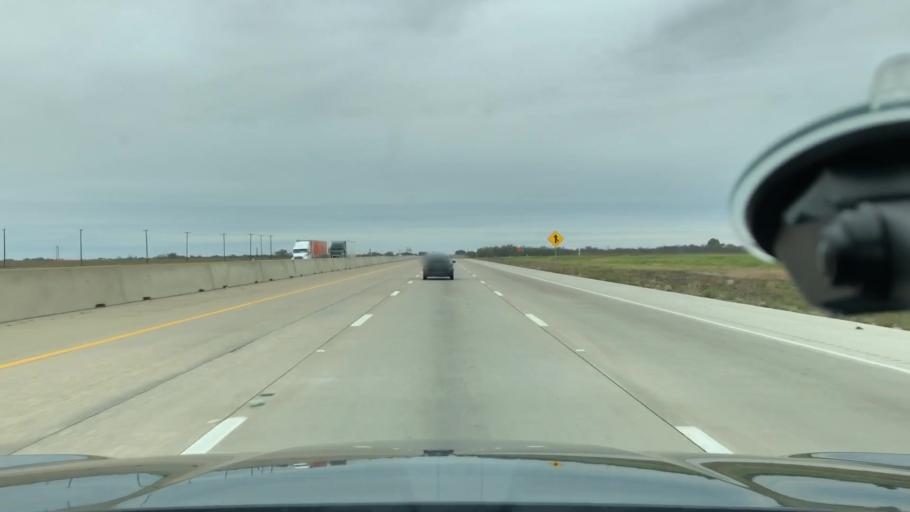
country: US
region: Texas
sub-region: Ellis County
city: Nash
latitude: 32.2600
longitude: -96.8728
